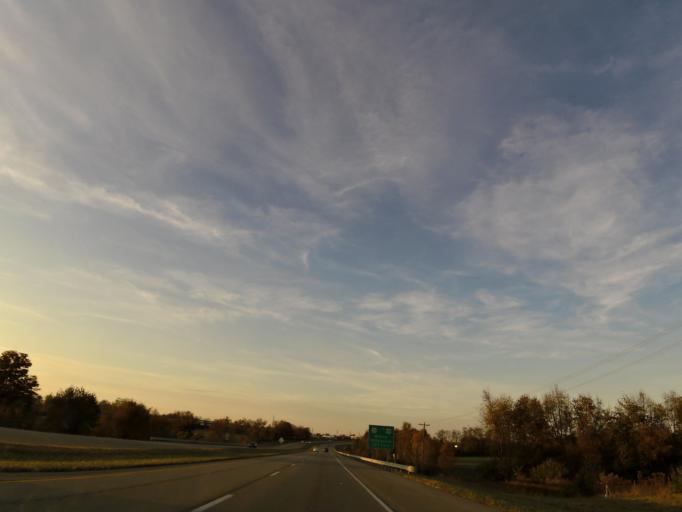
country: US
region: Kentucky
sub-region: Jessamine County
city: Nicholasville
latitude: 37.8647
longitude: -84.5948
